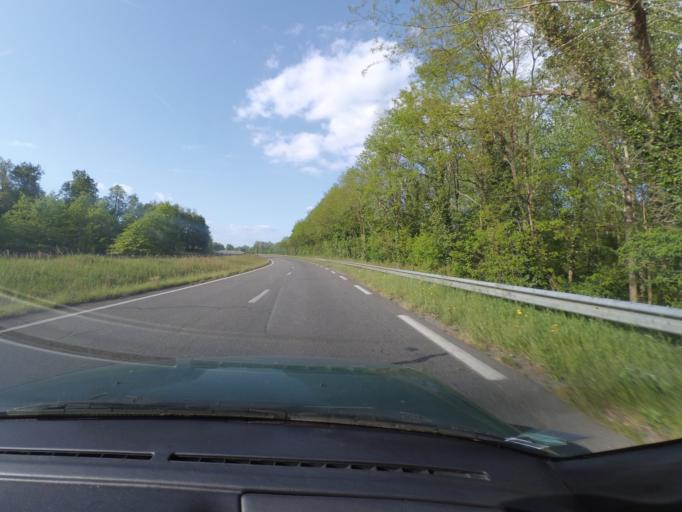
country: FR
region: Pays de la Loire
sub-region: Departement de la Vendee
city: Saligny
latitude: 46.8217
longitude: -1.4293
